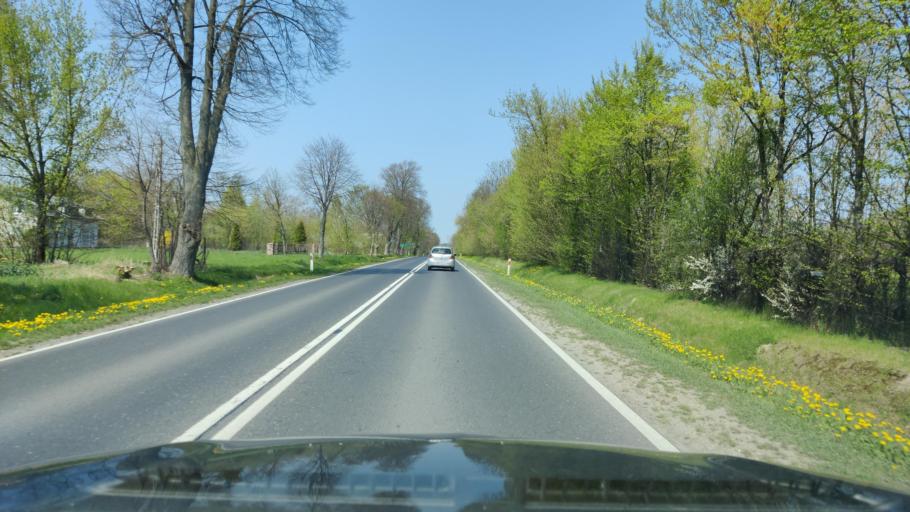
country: PL
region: Masovian Voivodeship
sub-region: Powiat pultuski
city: Pultusk
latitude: 52.6444
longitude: 21.0914
